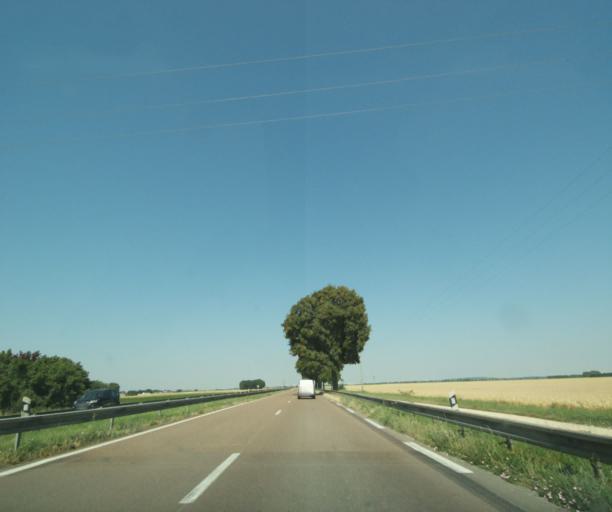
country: FR
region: Champagne-Ardenne
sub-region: Departement de la Marne
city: Frignicourt
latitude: 48.6912
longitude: 4.7121
